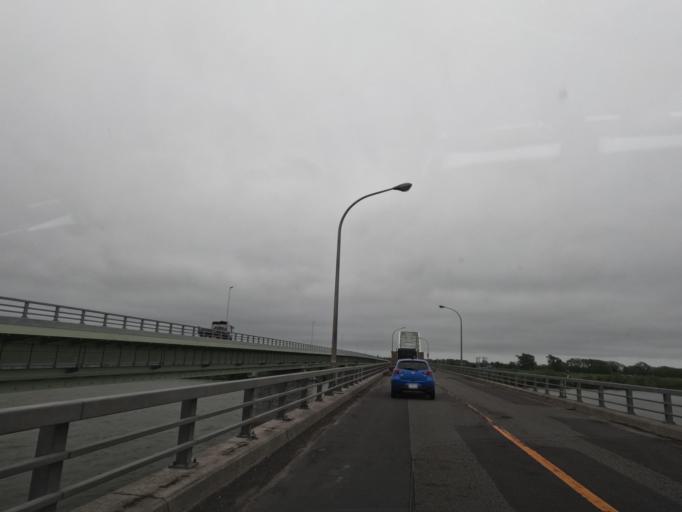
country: JP
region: Hokkaido
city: Ebetsu
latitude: 43.1344
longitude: 141.5103
